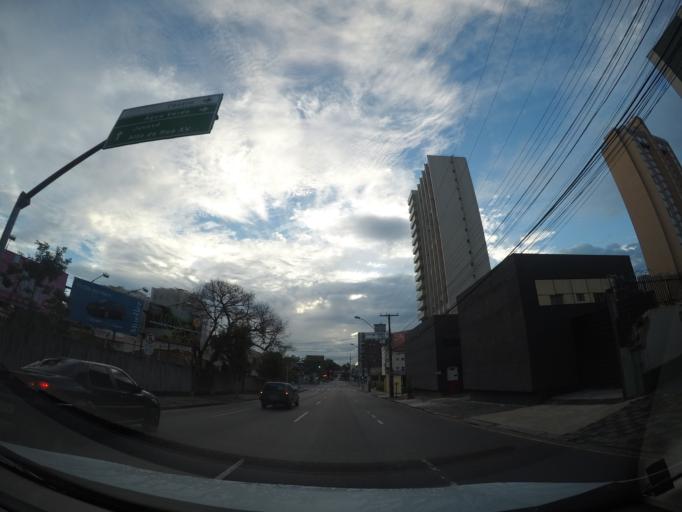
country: BR
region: Parana
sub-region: Curitiba
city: Curitiba
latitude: -25.4295
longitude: -49.2876
